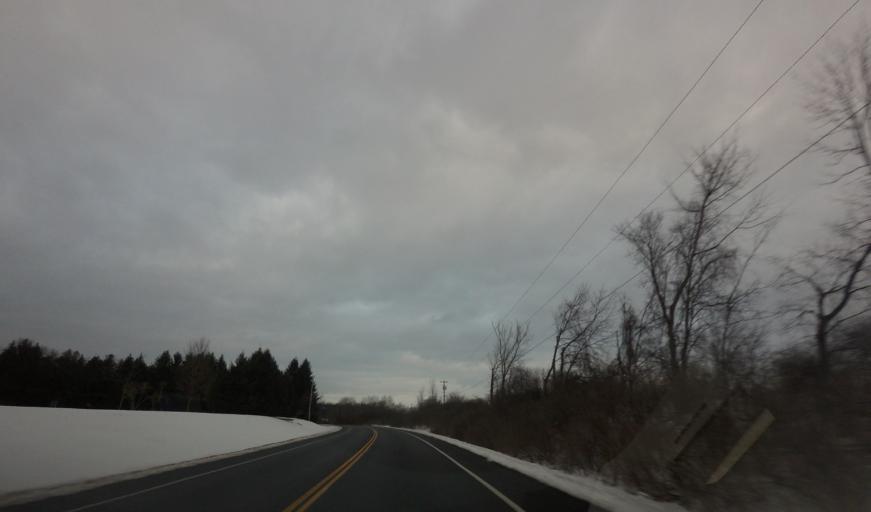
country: US
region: New York
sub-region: Tompkins County
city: Dryden
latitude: 42.5371
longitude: -76.3016
